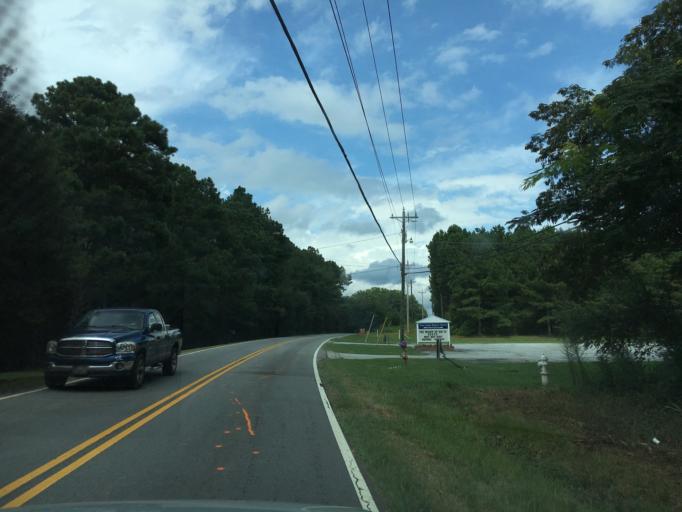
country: US
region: Georgia
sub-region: Rockdale County
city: Lakeview Estates
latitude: 33.7570
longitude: -84.0159
